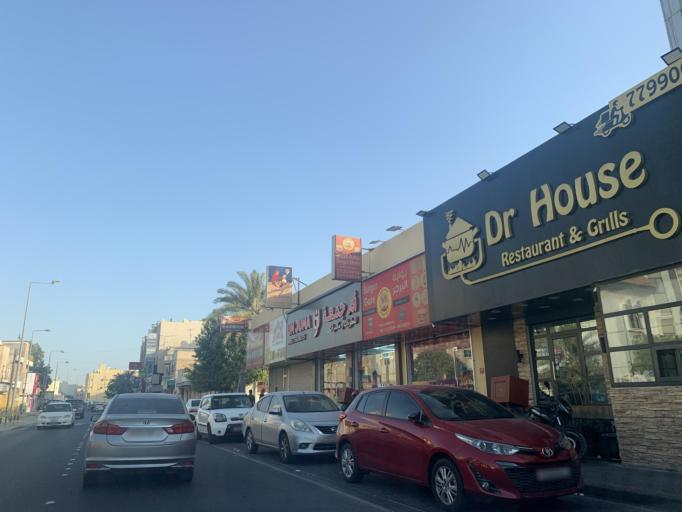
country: BH
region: Manama
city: Jidd Hafs
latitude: 26.2112
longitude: 50.4514
